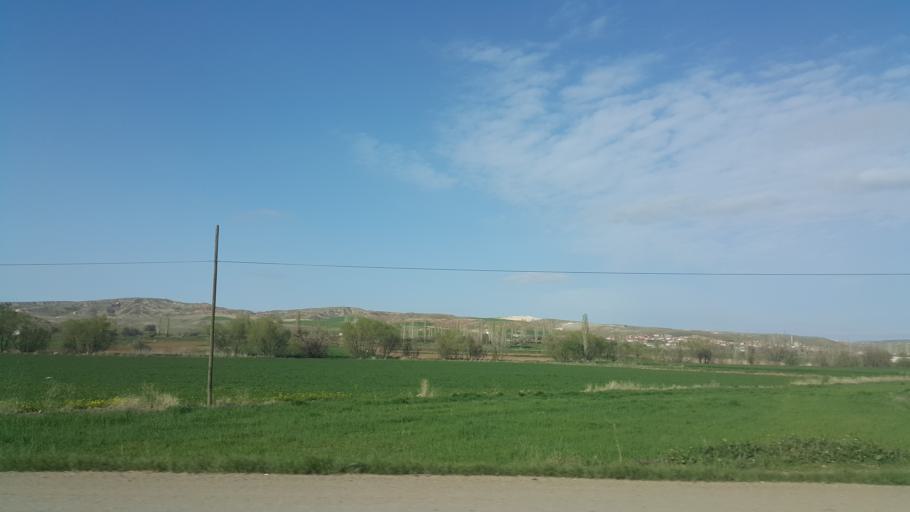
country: TR
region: Aksaray
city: Acipinar
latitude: 38.4821
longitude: 33.8893
